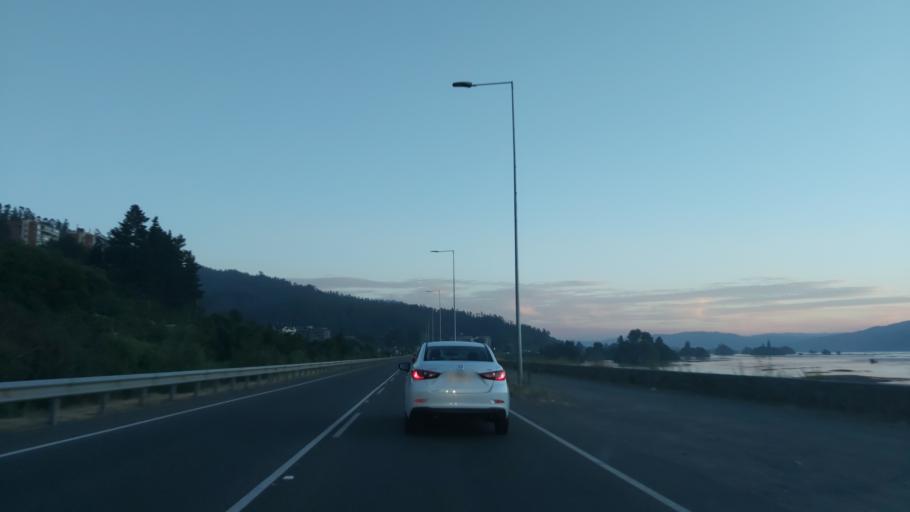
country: CL
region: Biobio
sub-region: Provincia de Concepcion
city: Concepcion
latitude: -36.8736
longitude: -73.0423
